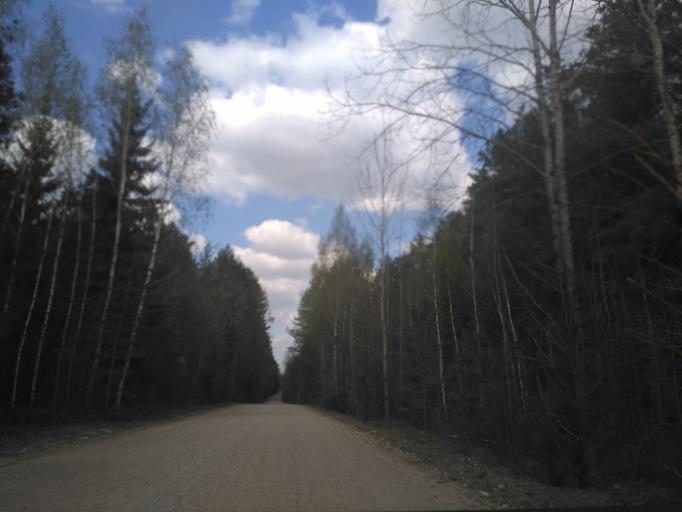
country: BY
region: Minsk
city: Il'ya
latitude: 54.2976
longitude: 27.2775
